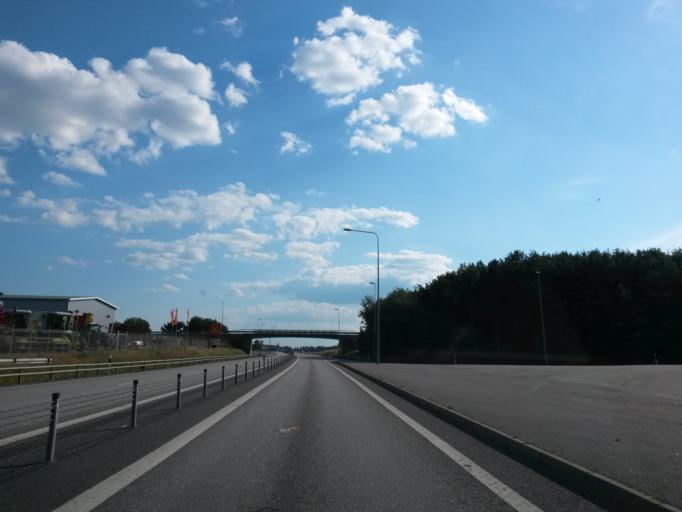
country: SE
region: Vaestra Goetaland
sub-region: Vara Kommun
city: Vara
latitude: 58.2797
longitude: 13.0208
